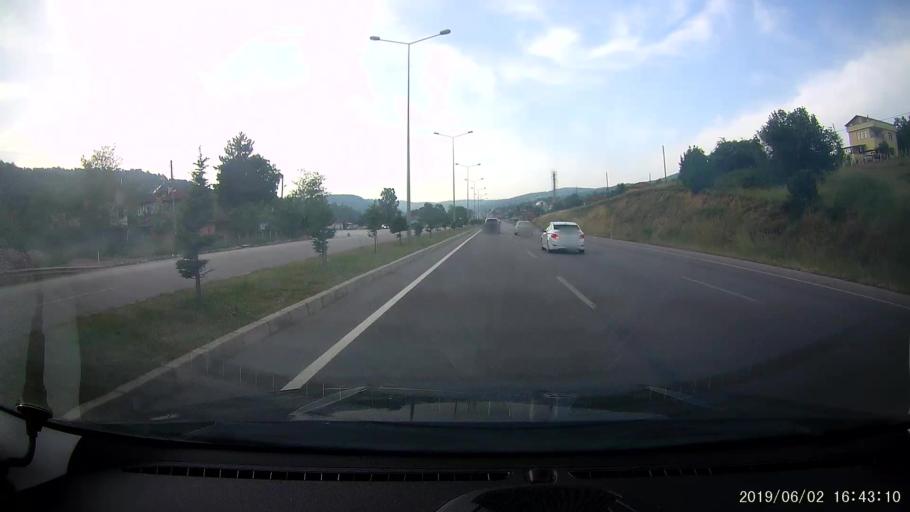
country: TR
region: Samsun
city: Kavak
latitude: 41.1309
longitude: 36.1326
